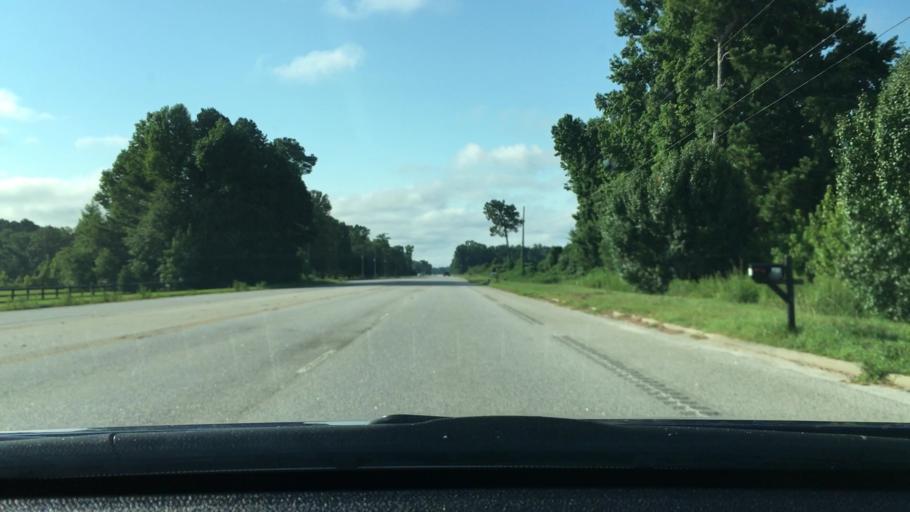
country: US
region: South Carolina
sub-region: Clarendon County
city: Manning
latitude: 33.7672
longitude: -80.2338
